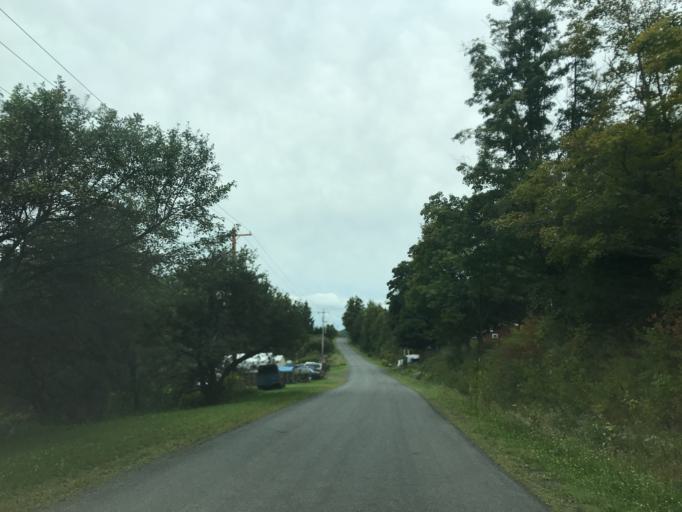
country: US
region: New York
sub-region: Otsego County
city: Worcester
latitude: 42.5747
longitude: -74.6717
